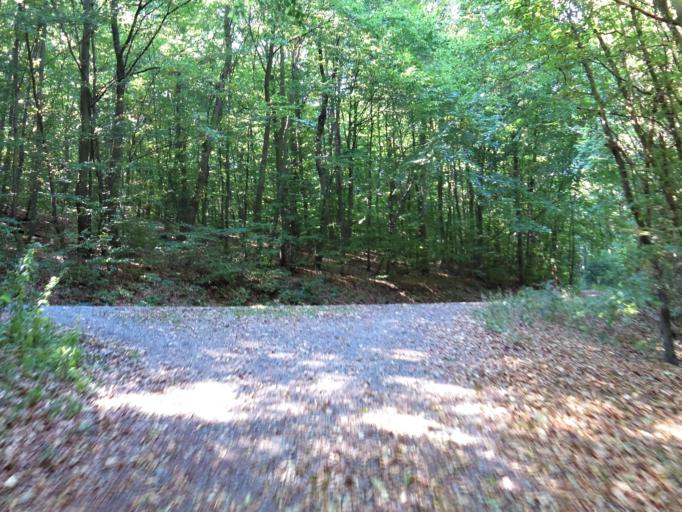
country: DE
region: Bavaria
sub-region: Regierungsbezirk Unterfranken
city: Wuerzburg
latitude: 49.7688
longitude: 9.9005
